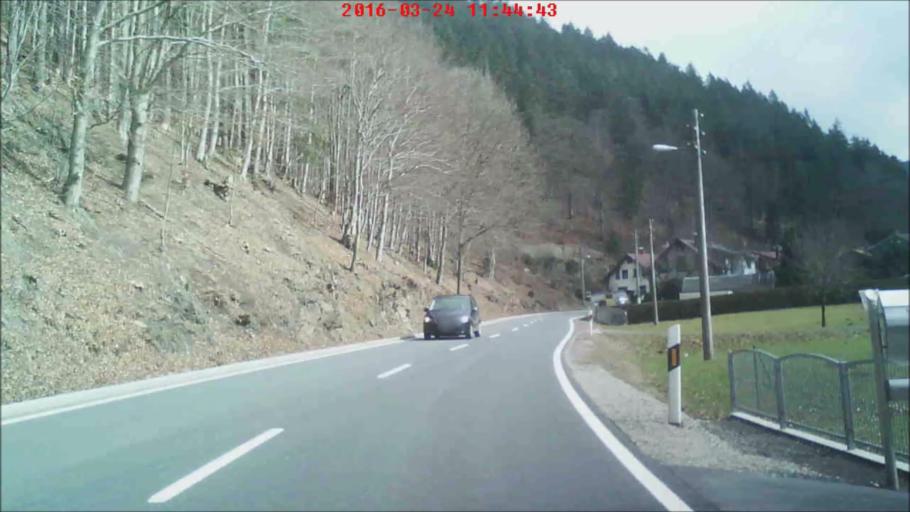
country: DE
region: Thuringia
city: Bachfeld
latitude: 50.4574
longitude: 10.9830
